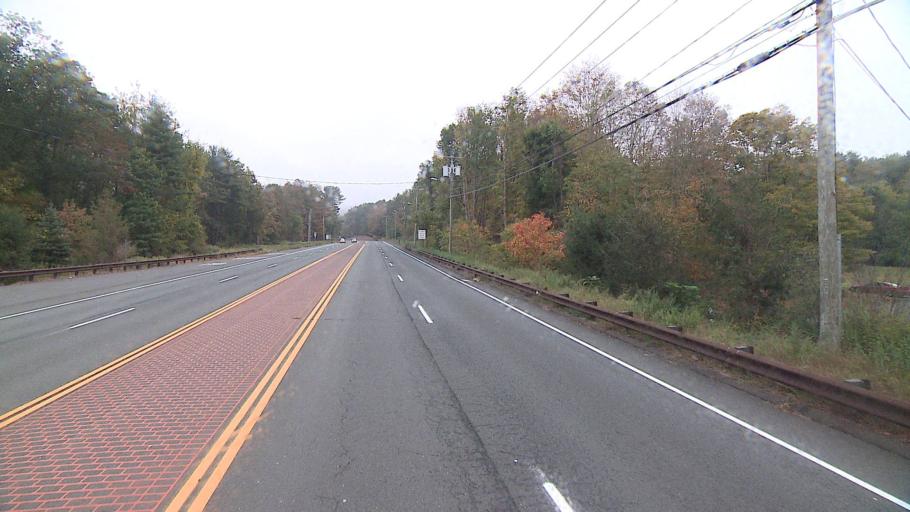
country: US
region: Connecticut
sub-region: Hartford County
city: Weatogue
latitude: 41.8048
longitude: -72.8147
